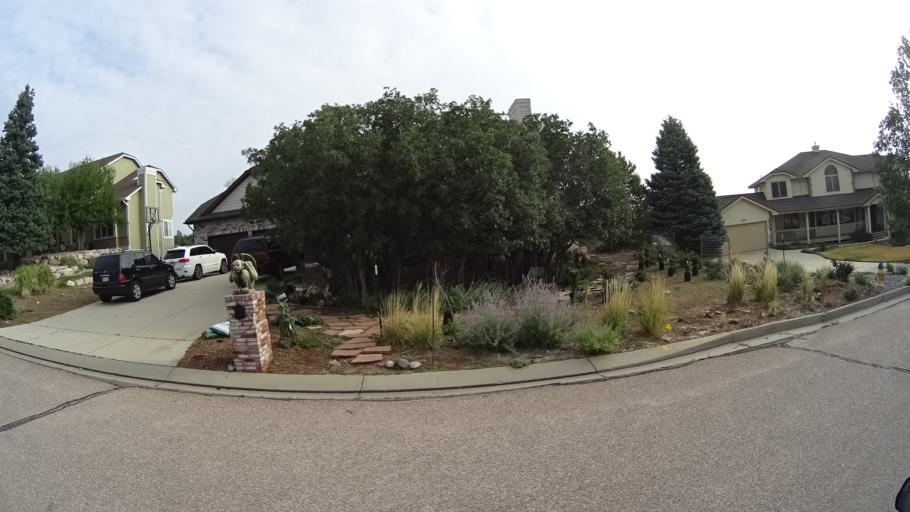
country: US
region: Colorado
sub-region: El Paso County
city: Air Force Academy
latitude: 38.9312
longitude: -104.8583
